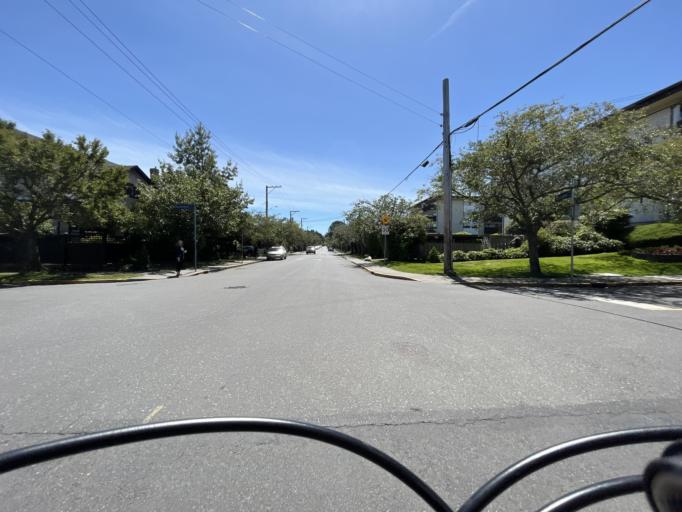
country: CA
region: British Columbia
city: Victoria
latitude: 48.4158
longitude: -123.3594
